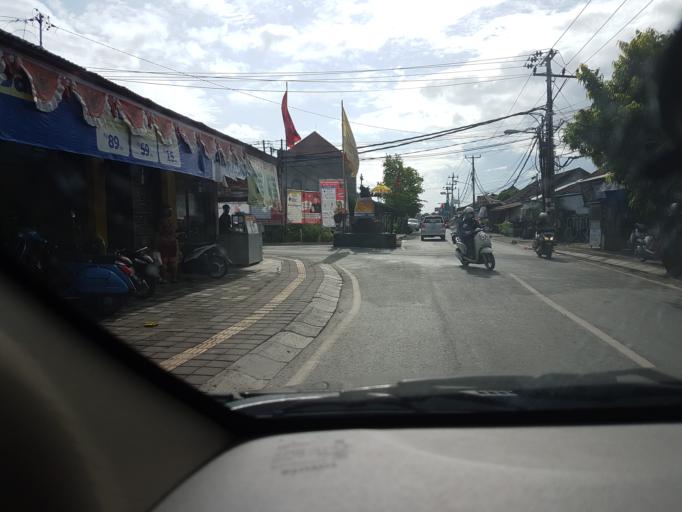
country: ID
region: Bali
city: Kuta
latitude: -8.6799
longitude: 115.1803
